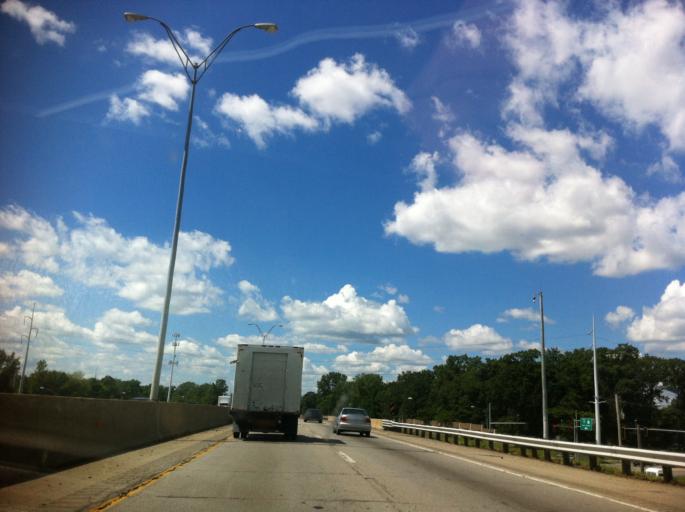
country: US
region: Ohio
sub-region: Lucas County
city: Ottawa Hills
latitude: 41.6864
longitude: -83.6220
